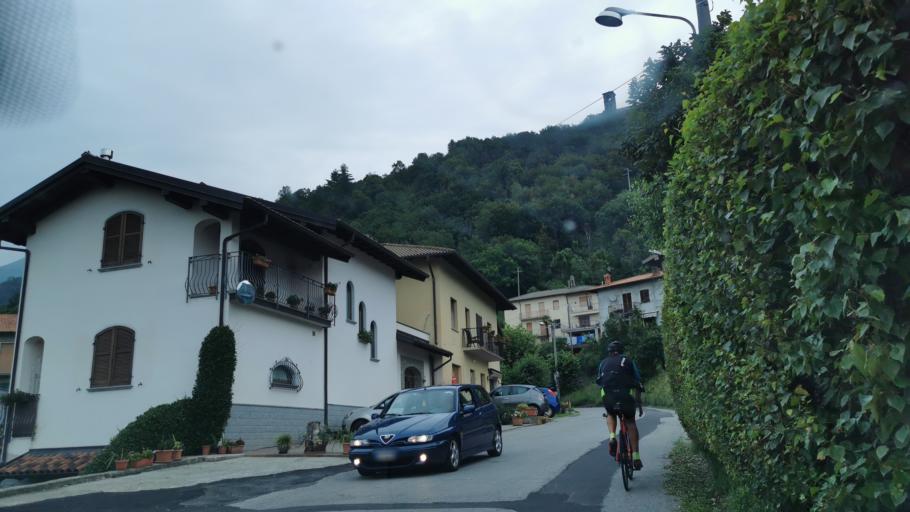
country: IT
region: Lombardy
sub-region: Provincia di Como
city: Peglio
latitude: 46.1534
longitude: 9.2976
